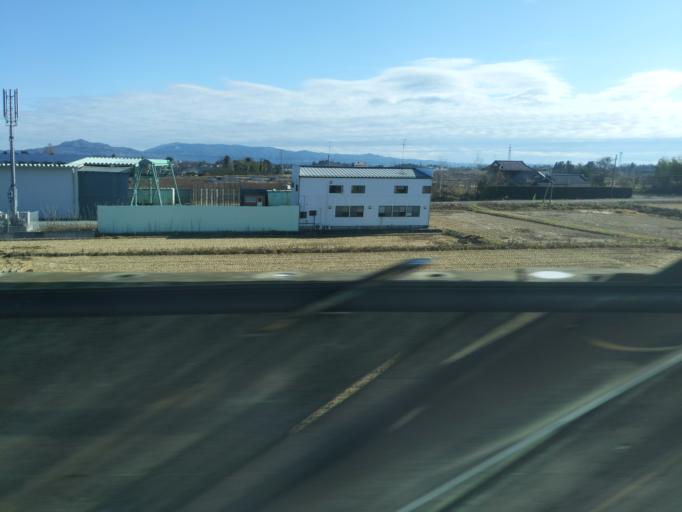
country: JP
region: Fukushima
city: Sukagawa
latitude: 37.3109
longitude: 140.3479
